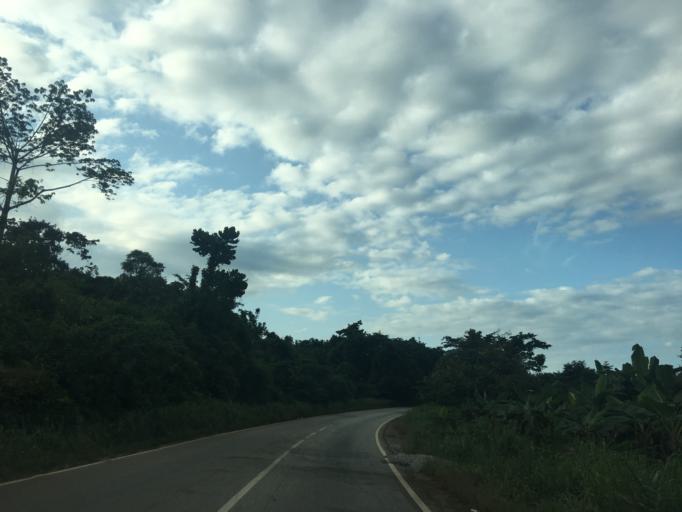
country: GH
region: Western
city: Bibiani
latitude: 6.4139
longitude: -2.3029
